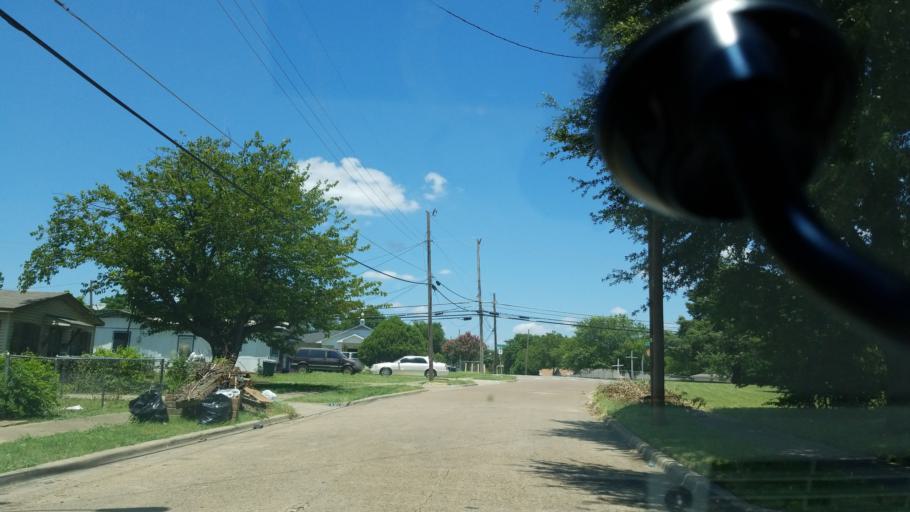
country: US
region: Texas
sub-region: Dallas County
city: Cockrell Hill
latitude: 32.6907
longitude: -96.8119
